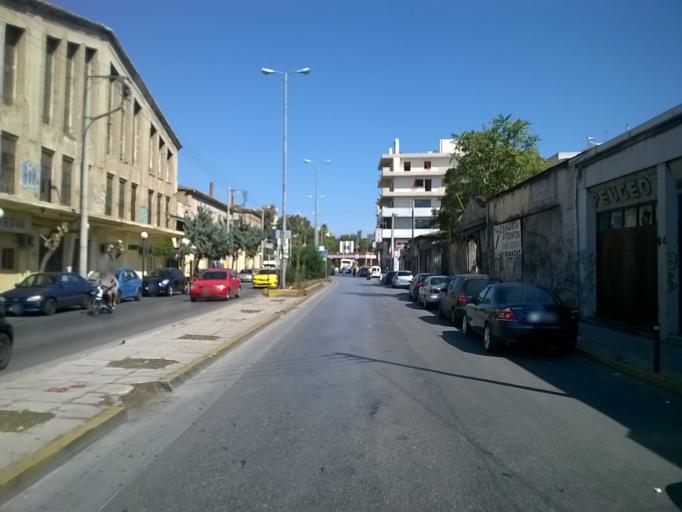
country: GR
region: Attica
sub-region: Nomos Attikis
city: Piraeus
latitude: 37.9533
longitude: 23.6478
